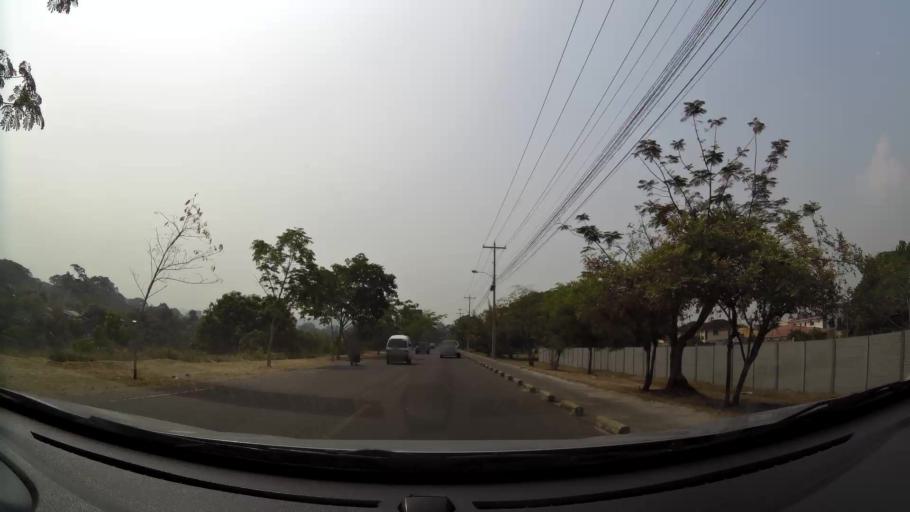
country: HN
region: Cortes
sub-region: San Pedro Sula
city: Pena Blanca
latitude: 15.5563
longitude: -88.0149
